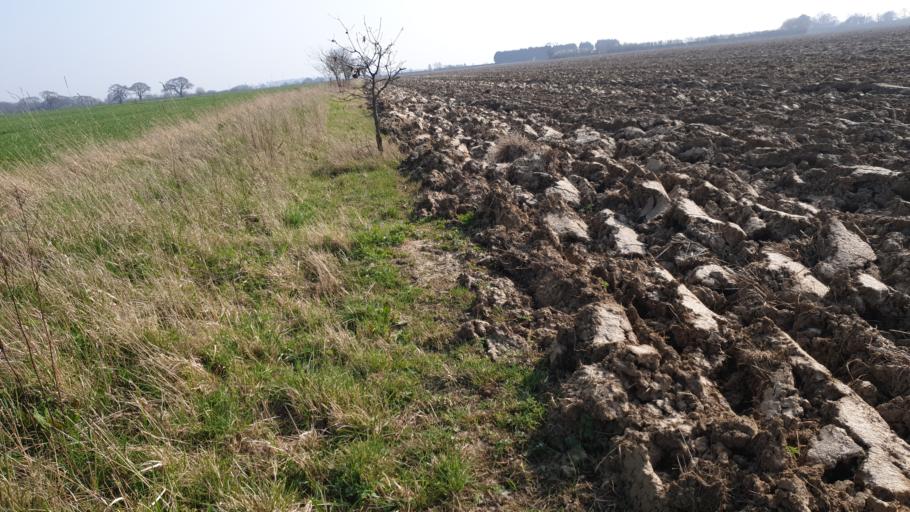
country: GB
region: England
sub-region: Essex
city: Mistley
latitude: 51.9062
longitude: 1.1274
